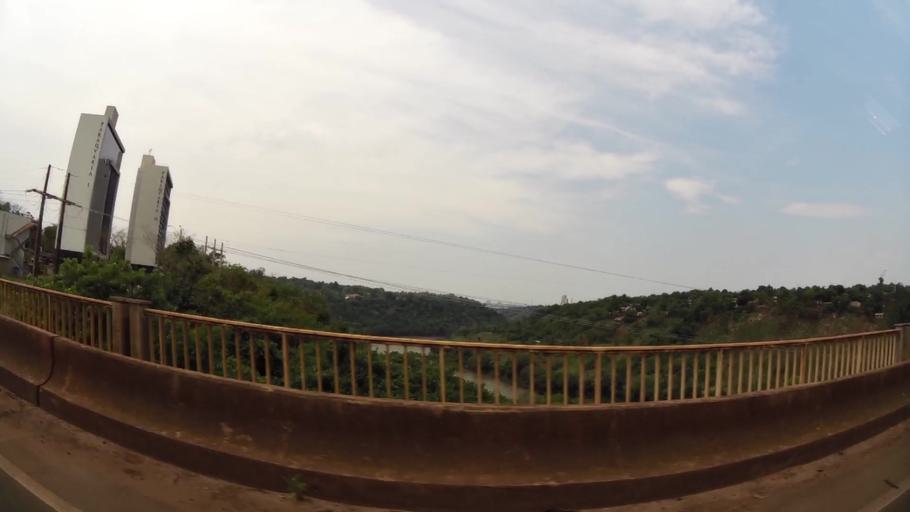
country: PY
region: Alto Parana
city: Ciudad del Este
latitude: -25.4898
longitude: -54.6305
